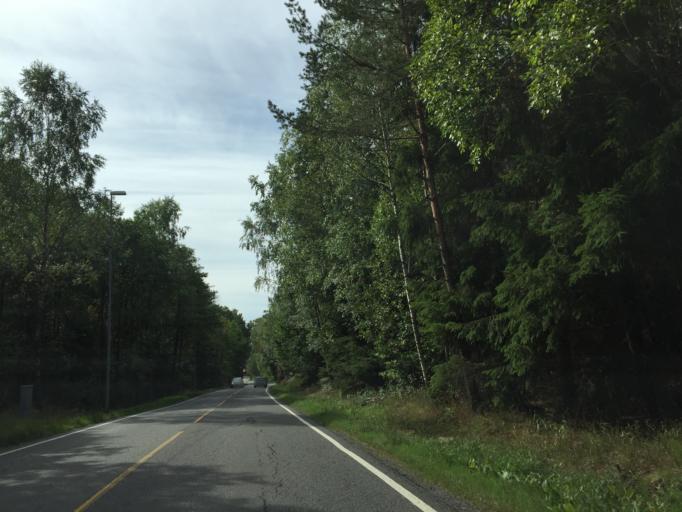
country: NO
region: Ostfold
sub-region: Moss
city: Moss
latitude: 59.4869
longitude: 10.6981
